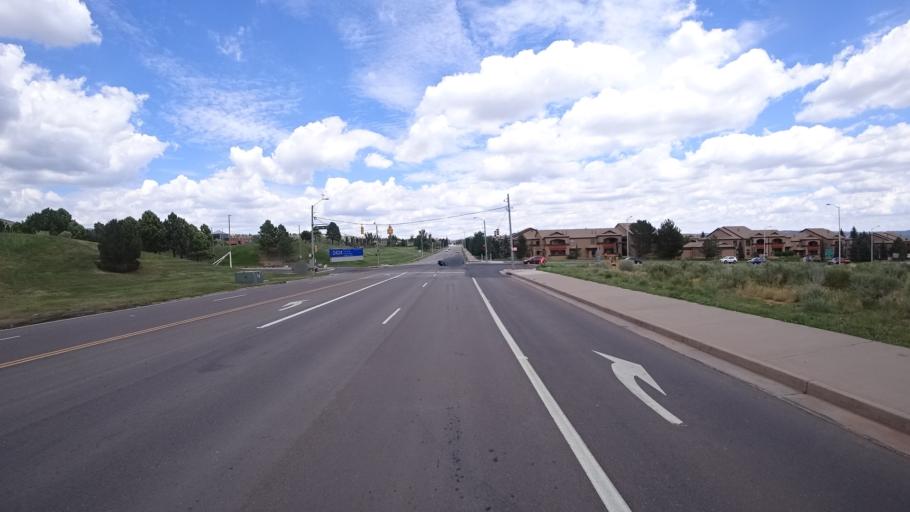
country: US
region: Colorado
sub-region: El Paso County
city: Manitou Springs
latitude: 38.8974
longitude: -104.8727
